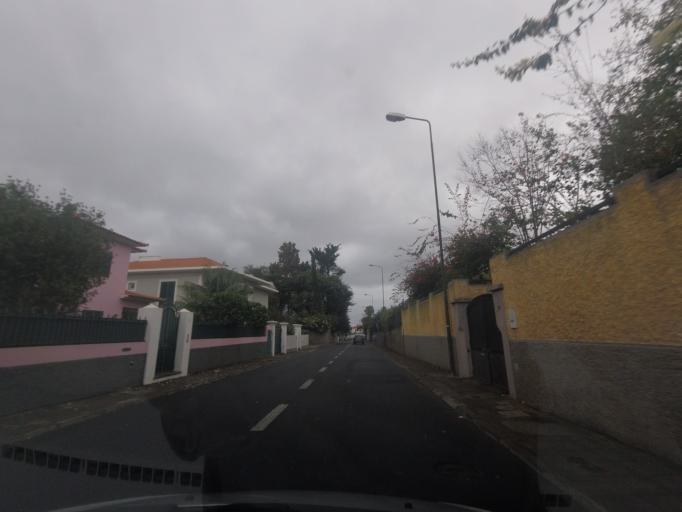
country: PT
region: Madeira
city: Camara de Lobos
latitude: 32.6534
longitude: -16.9354
